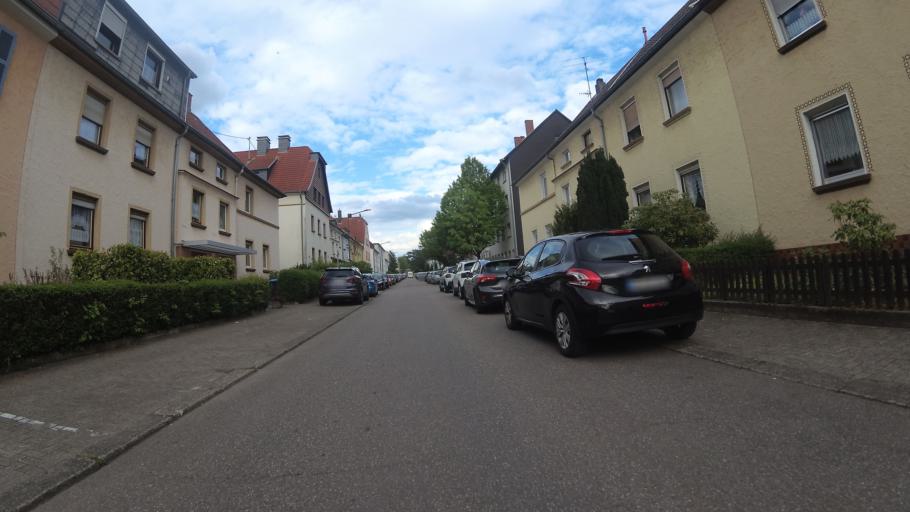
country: DE
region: Saarland
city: Neunkirchen
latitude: 49.3487
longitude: 7.1966
